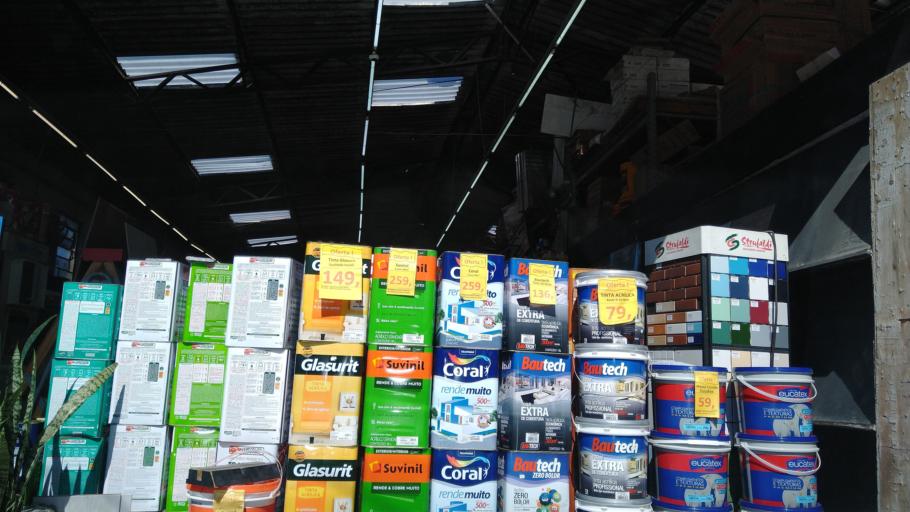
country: BR
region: Sao Paulo
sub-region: Guarulhos
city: Guarulhos
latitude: -23.5027
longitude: -46.5735
